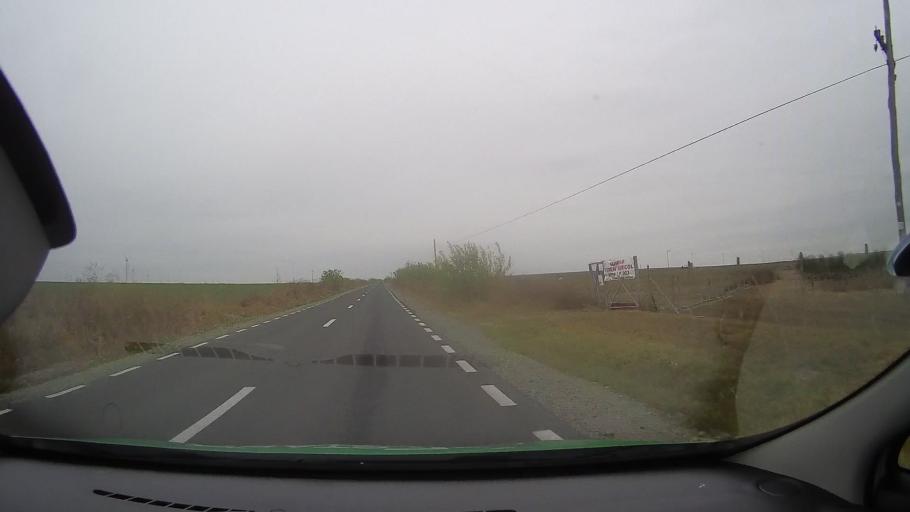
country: RO
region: Constanta
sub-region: Comuna Tortoman
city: Tortoman
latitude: 44.3679
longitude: 28.2077
